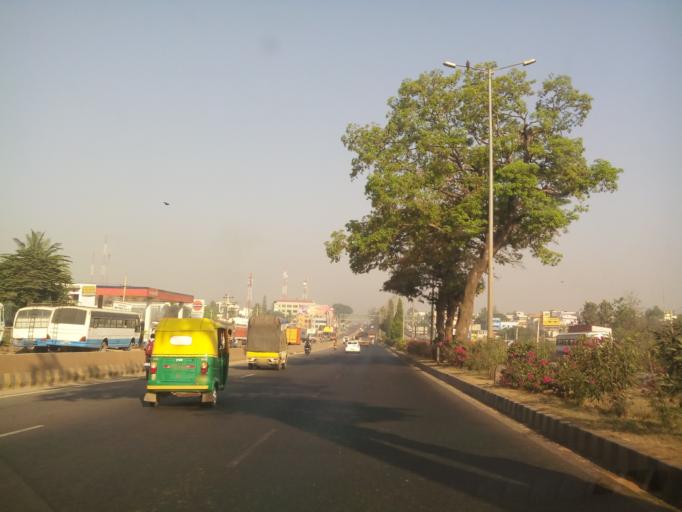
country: IN
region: Karnataka
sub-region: Bangalore Rural
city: Nelamangala
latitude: 13.0633
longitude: 77.4576
